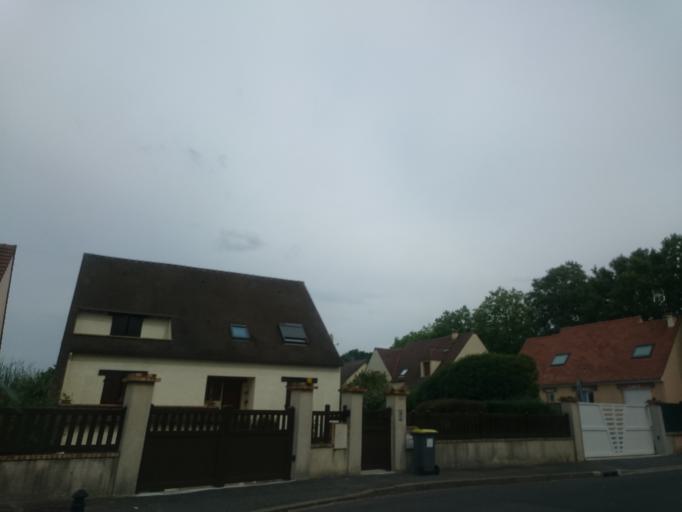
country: FR
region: Ile-de-France
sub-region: Departement de l'Essonne
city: Evry
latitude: 48.6240
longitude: 2.4577
